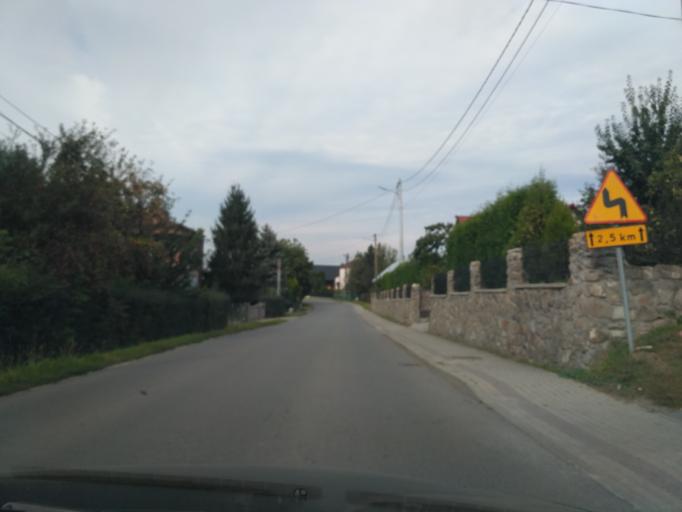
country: PL
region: Subcarpathian Voivodeship
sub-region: Powiat rzeszowski
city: Swilcza
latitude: 50.0726
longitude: 21.9004
